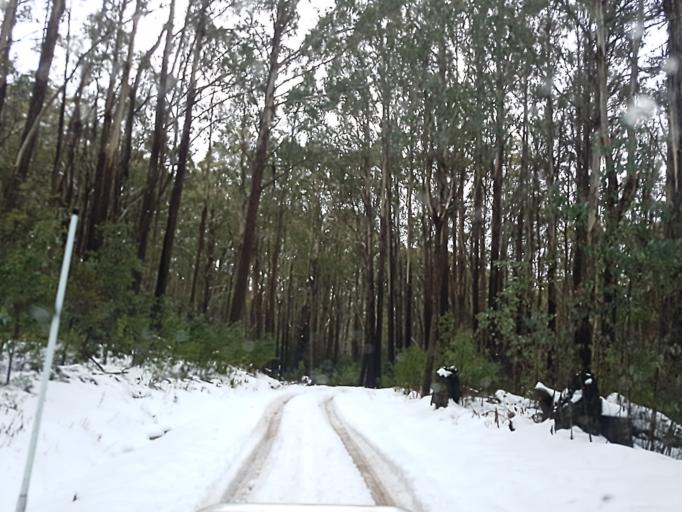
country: AU
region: Victoria
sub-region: Murrindindi
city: Alexandra
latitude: -37.4718
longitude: 145.8959
